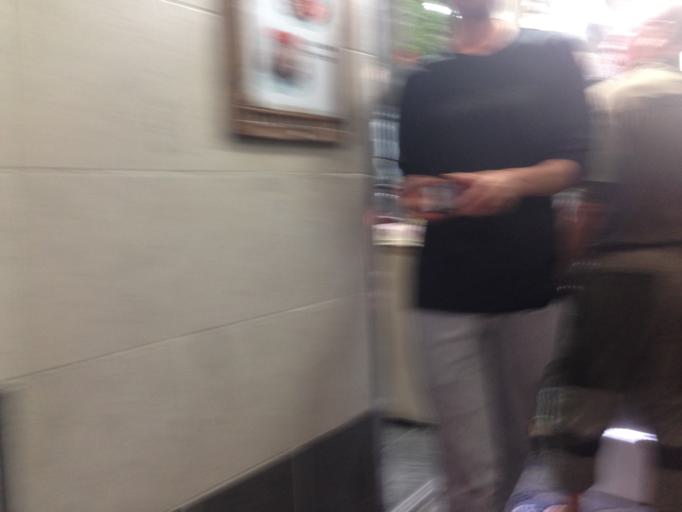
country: KR
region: Seoul
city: Seoul
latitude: 37.5700
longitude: 126.9913
